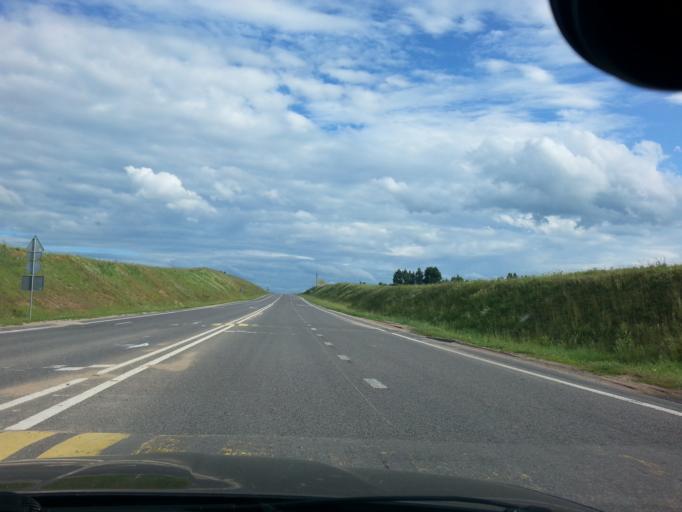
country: BY
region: Grodnenskaya
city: Astravyets
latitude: 54.7804
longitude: 26.0536
